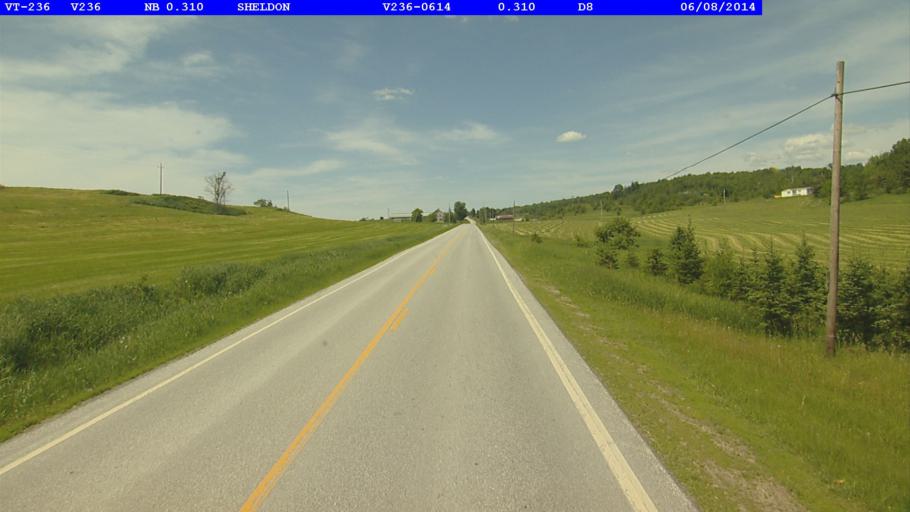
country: US
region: Vermont
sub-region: Franklin County
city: Enosburg Falls
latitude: 44.9155
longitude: -72.8649
